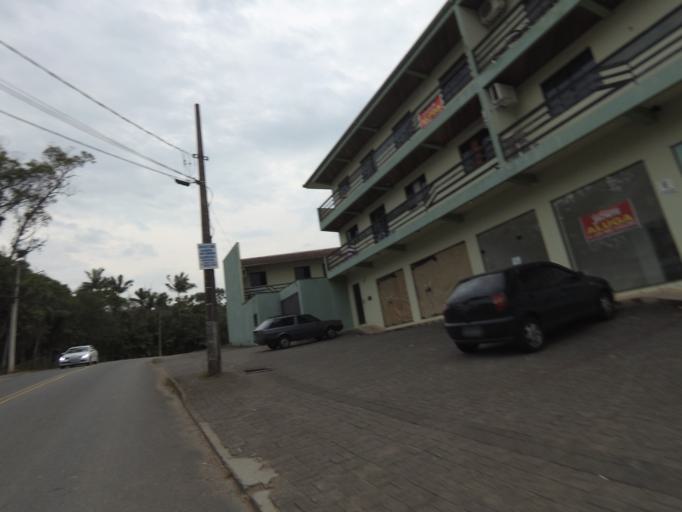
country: BR
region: Santa Catarina
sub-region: Blumenau
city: Blumenau
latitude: -26.8659
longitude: -49.0508
